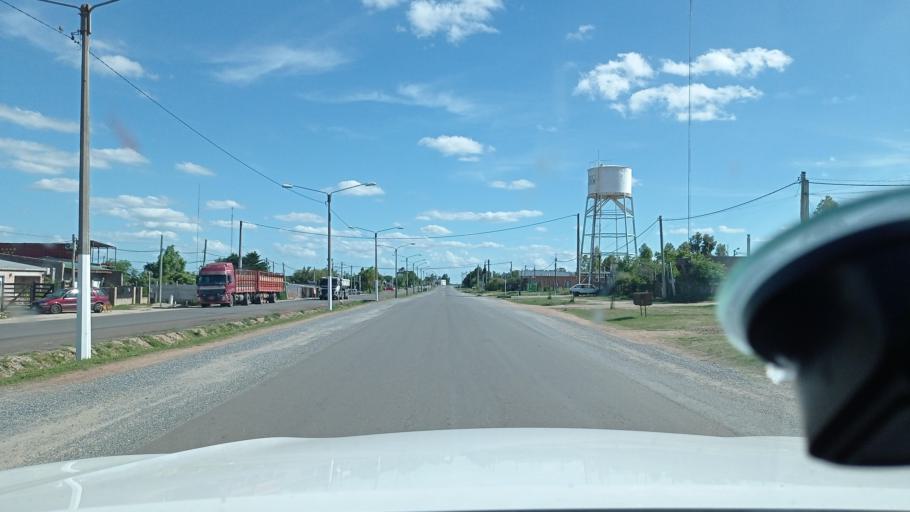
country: UY
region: Florida
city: Florida
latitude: -34.0860
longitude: -56.2373
